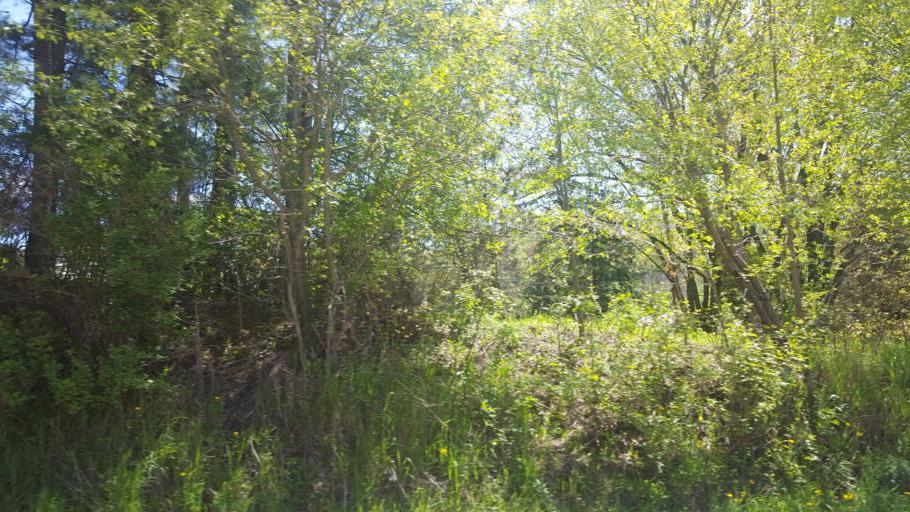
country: US
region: Wisconsin
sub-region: Vernon County
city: Hillsboro
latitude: 43.5789
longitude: -90.4066
